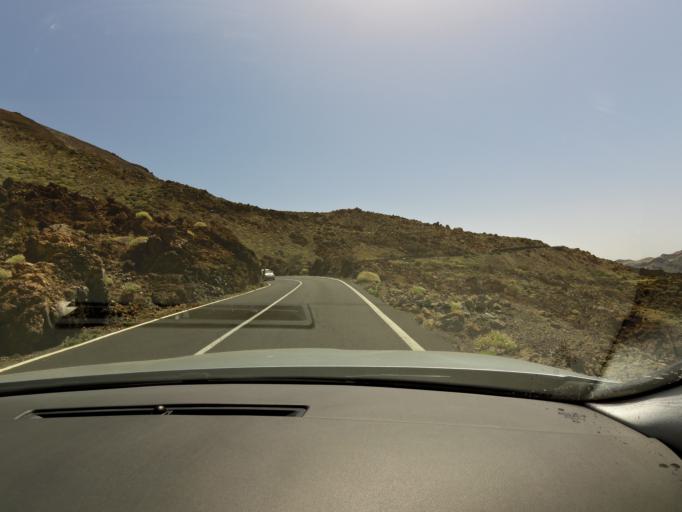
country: ES
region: Canary Islands
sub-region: Provincia de Santa Cruz de Tenerife
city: Vilaflor
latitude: 28.2587
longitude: -16.6161
